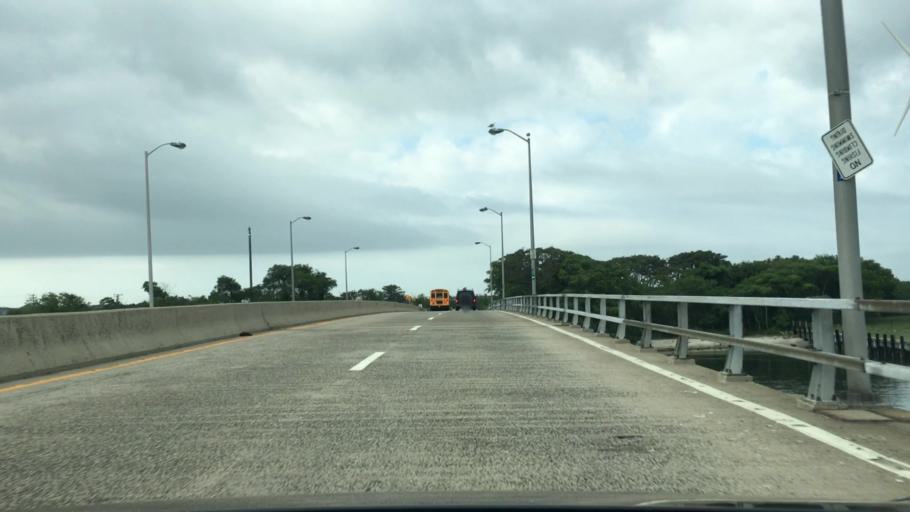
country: US
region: New York
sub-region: Nassau County
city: Point Lookout
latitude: 40.5945
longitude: -73.5873
